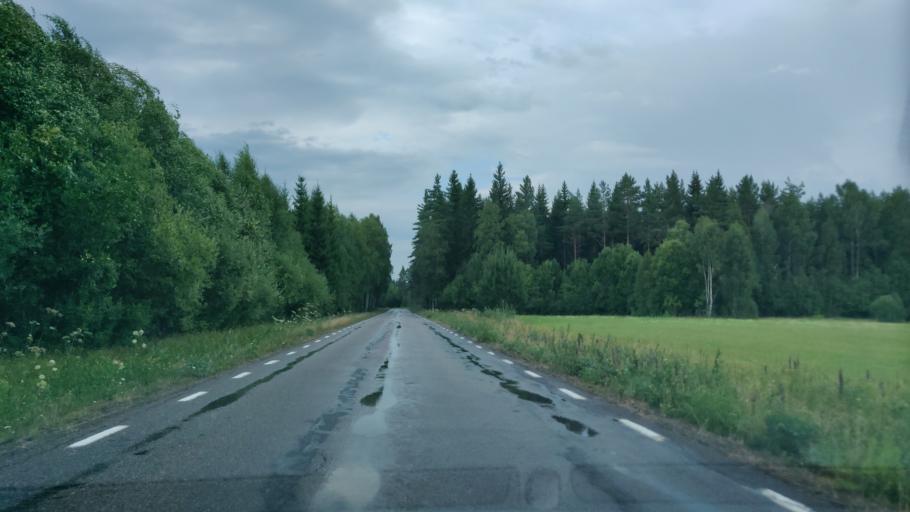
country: SE
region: Vaermland
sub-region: Munkfors Kommun
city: Munkfors
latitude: 59.8822
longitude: 13.5219
